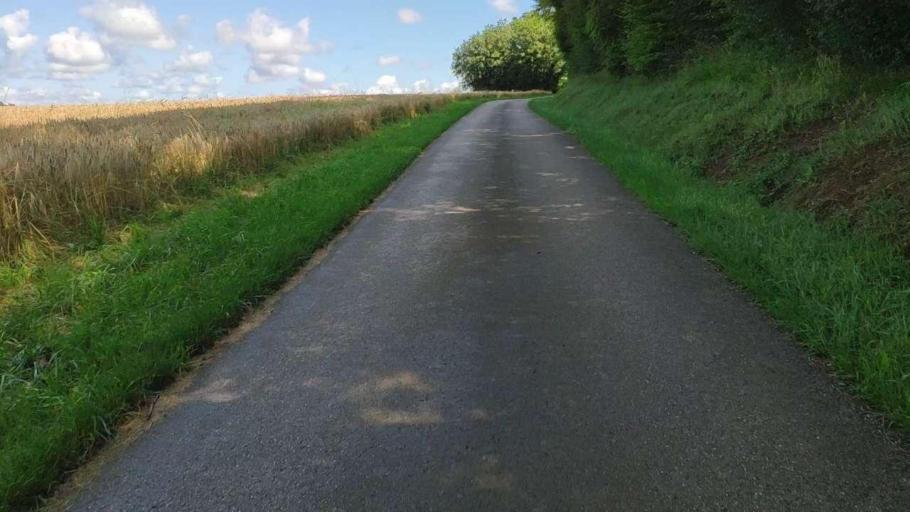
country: FR
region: Franche-Comte
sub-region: Departement du Jura
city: Bletterans
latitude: 46.8030
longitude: 5.5528
